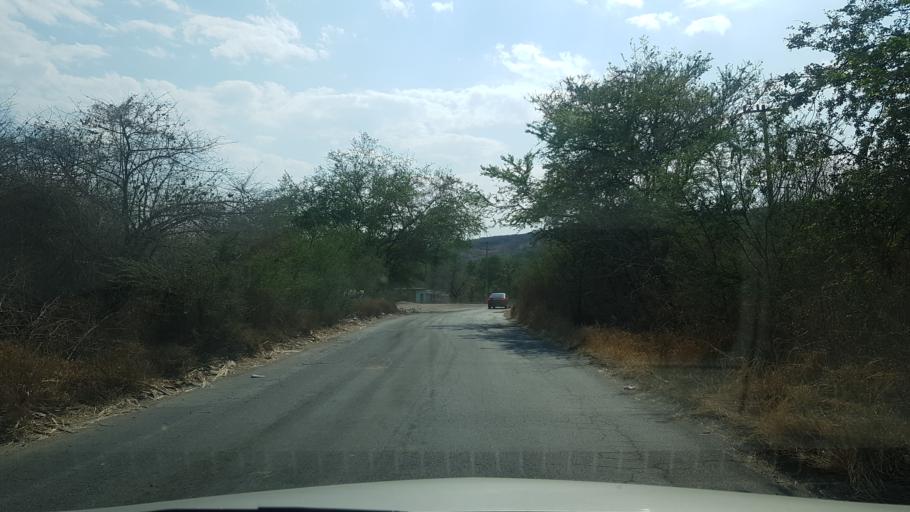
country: MX
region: Morelos
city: Ahuehuetzingo
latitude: 18.6478
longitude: -99.2976
